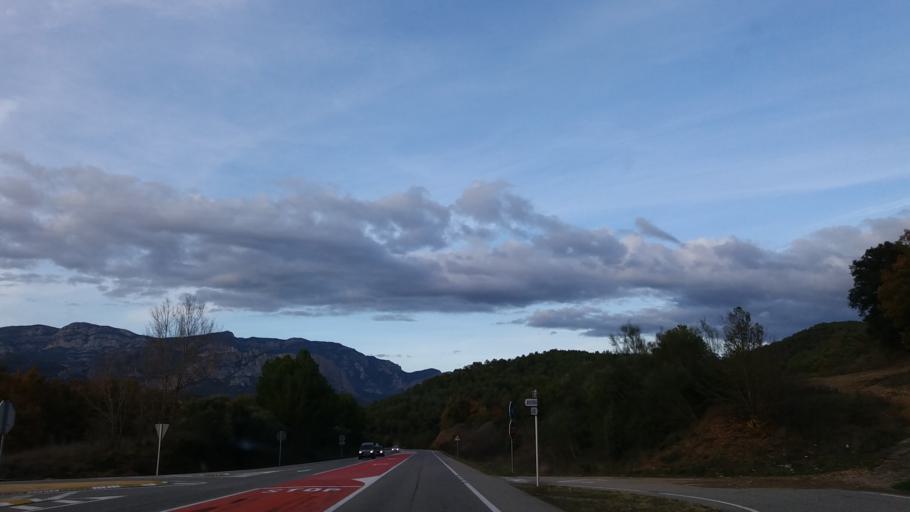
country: ES
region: Catalonia
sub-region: Provincia de Lleida
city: Oliana
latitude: 42.0276
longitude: 1.2947
